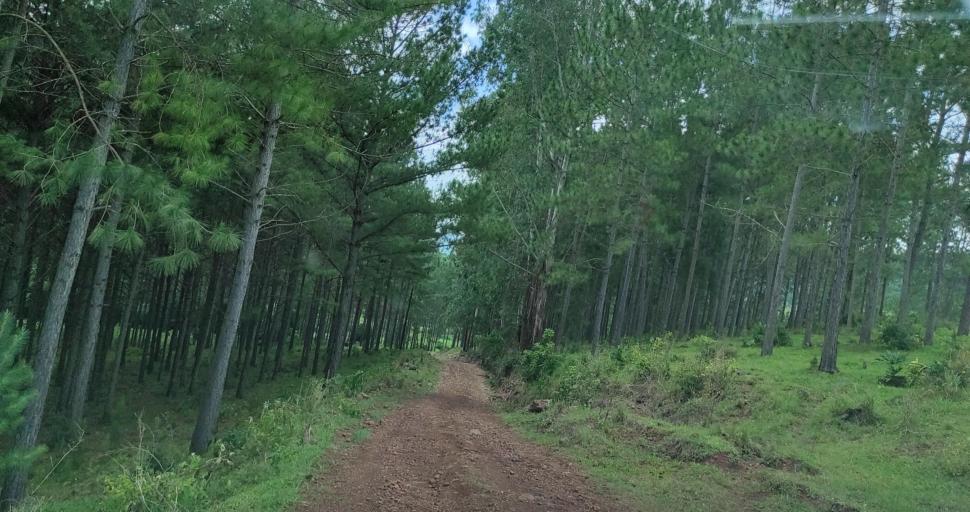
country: AR
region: Misiones
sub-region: Departamento de Veinticinco de Mayo
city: Veinticinco de Mayo
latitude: -27.4178
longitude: -54.7143
